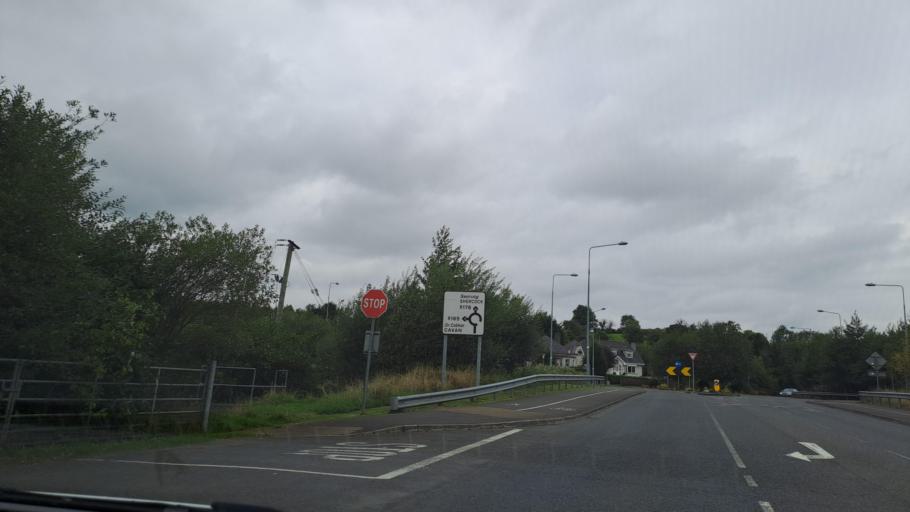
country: IE
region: Ulster
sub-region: An Cabhan
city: Bailieborough
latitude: 53.9195
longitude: -6.9693
